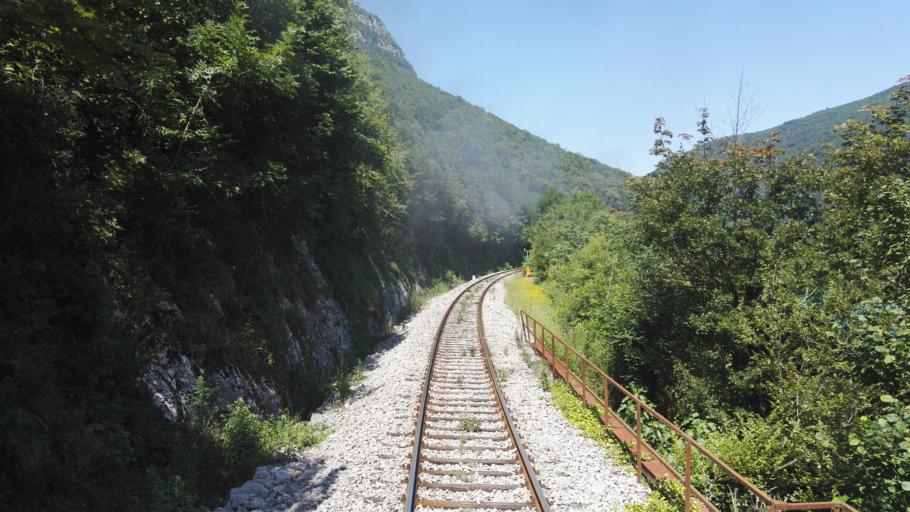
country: SI
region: Nova Gorica
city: Solkan
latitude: 45.9983
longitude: 13.6328
